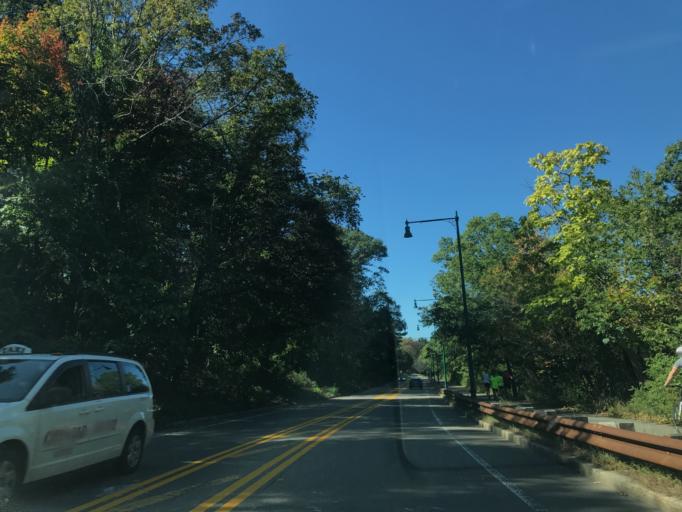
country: US
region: Massachusetts
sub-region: Middlesex County
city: Watertown
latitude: 42.3590
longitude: -71.1778
